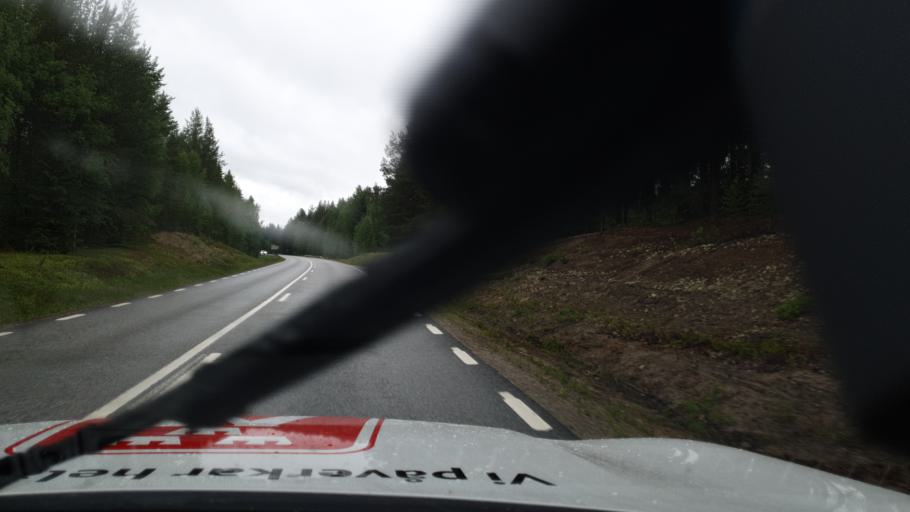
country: SE
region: Vaesterbotten
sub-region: Vindelns Kommun
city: Vindeln
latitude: 64.3592
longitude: 19.4516
